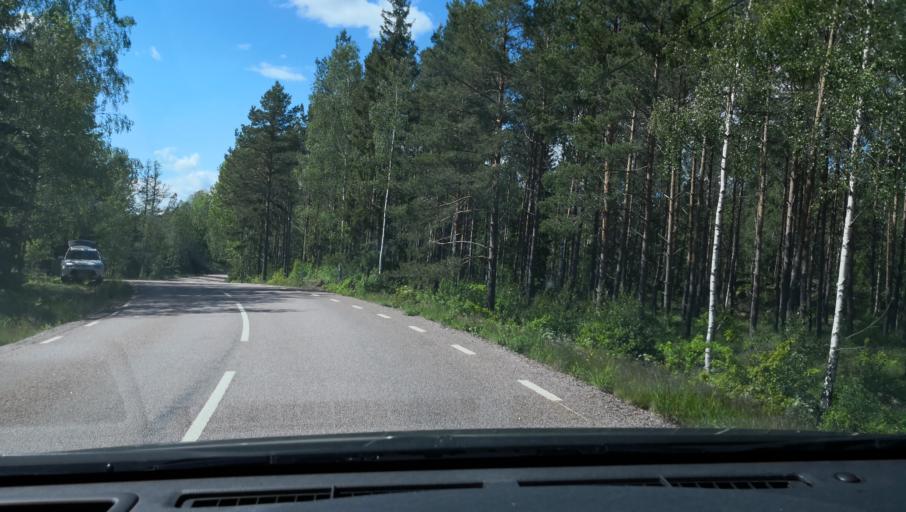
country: SE
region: Vaestmanland
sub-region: Arboga Kommun
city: Tyringe
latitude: 59.3040
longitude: 16.0148
